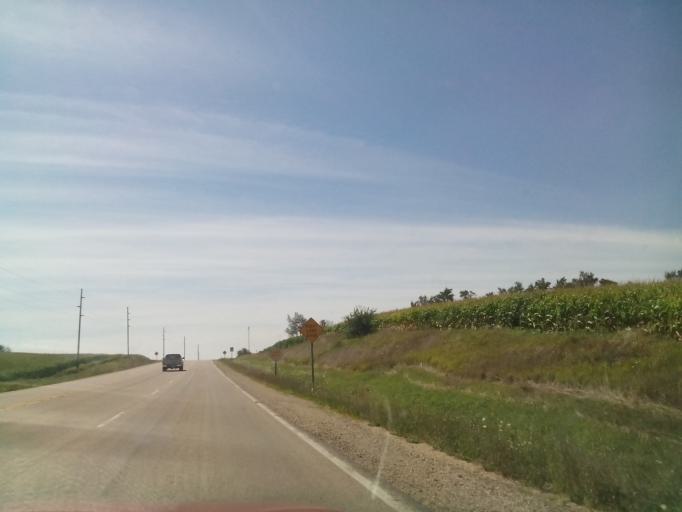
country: US
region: Wisconsin
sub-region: Green County
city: Monticello
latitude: 42.6779
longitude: -89.6169
